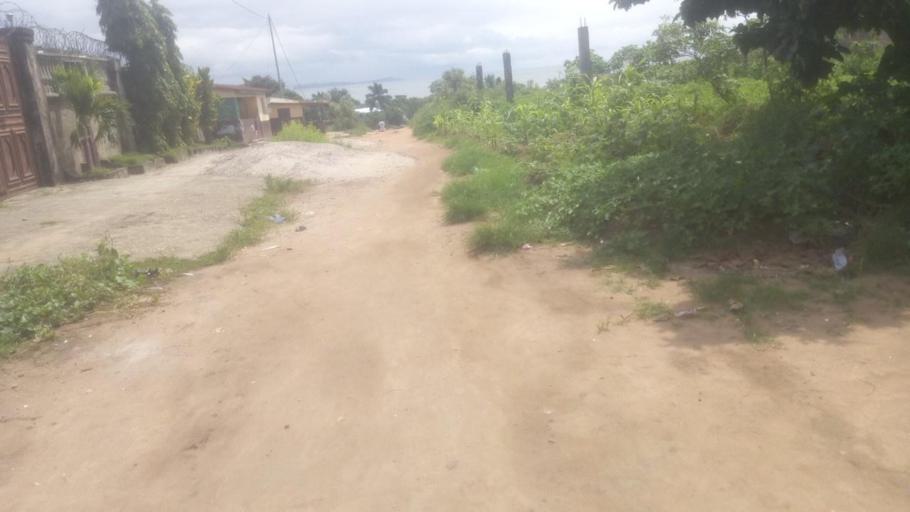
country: SL
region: Western Area
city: Freetown
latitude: 8.5234
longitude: -13.1520
